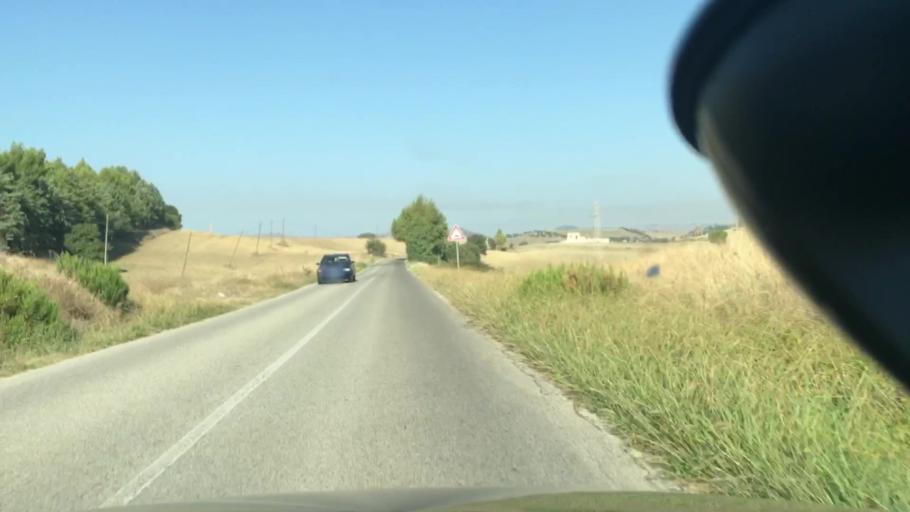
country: IT
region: Basilicate
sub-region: Provincia di Matera
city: La Martella
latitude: 40.6657
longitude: 16.4928
